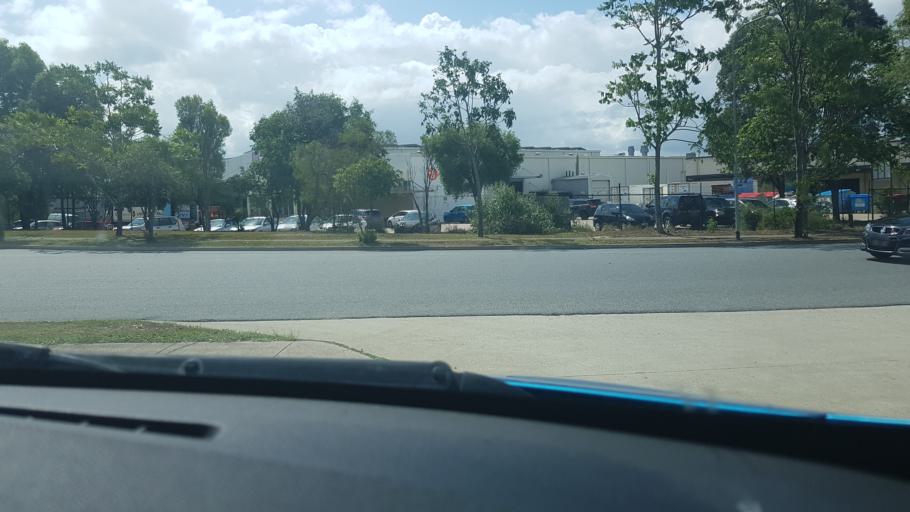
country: AU
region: Queensland
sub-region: Brisbane
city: Forest Lake
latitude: -27.6432
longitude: 152.9821
